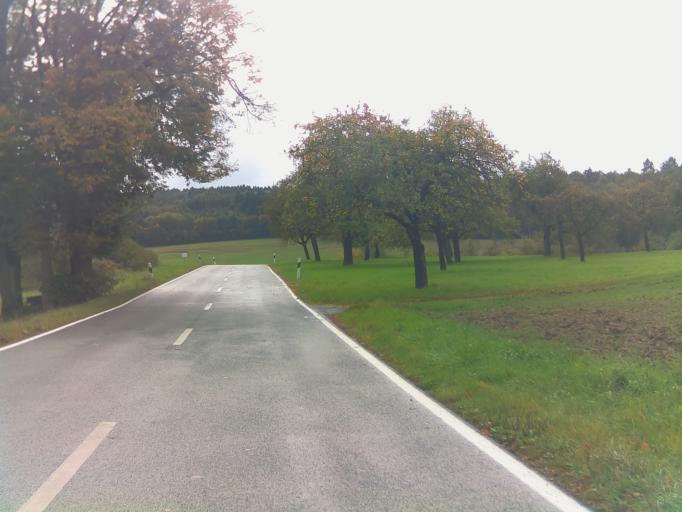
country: DE
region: Bavaria
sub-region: Upper Franconia
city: Zapfendorf
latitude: 50.0116
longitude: 10.9768
